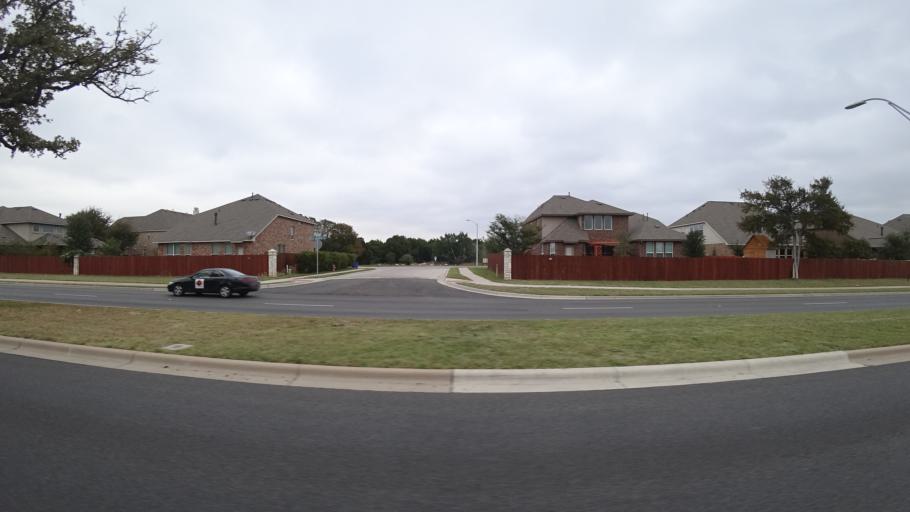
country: US
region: Texas
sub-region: Williamson County
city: Cedar Park
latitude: 30.4967
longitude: -97.8428
